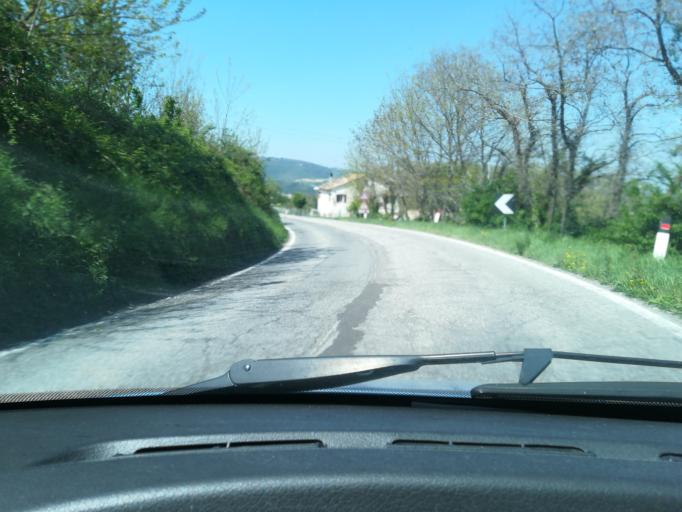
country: IT
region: The Marches
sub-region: Provincia di Macerata
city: Cingoli
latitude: 43.3869
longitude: 13.2070
